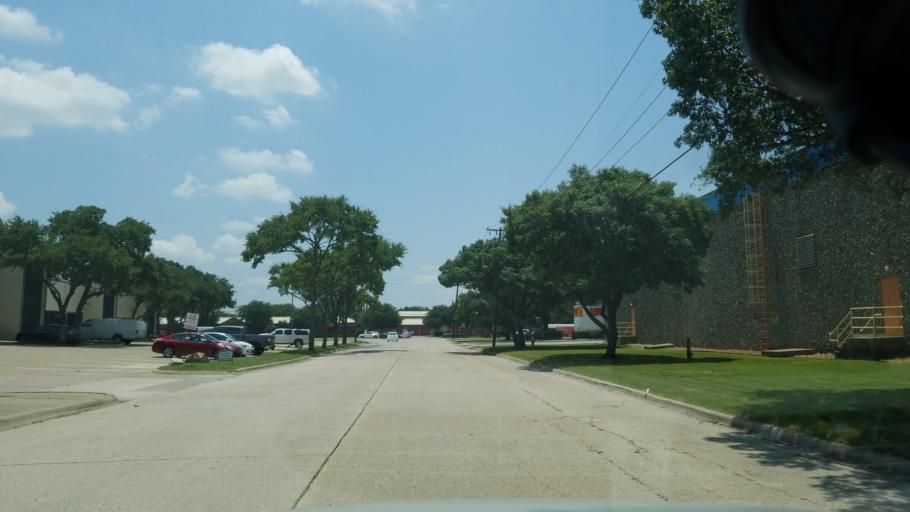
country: US
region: Texas
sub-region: Dallas County
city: Carrollton
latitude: 32.9550
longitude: -96.8796
